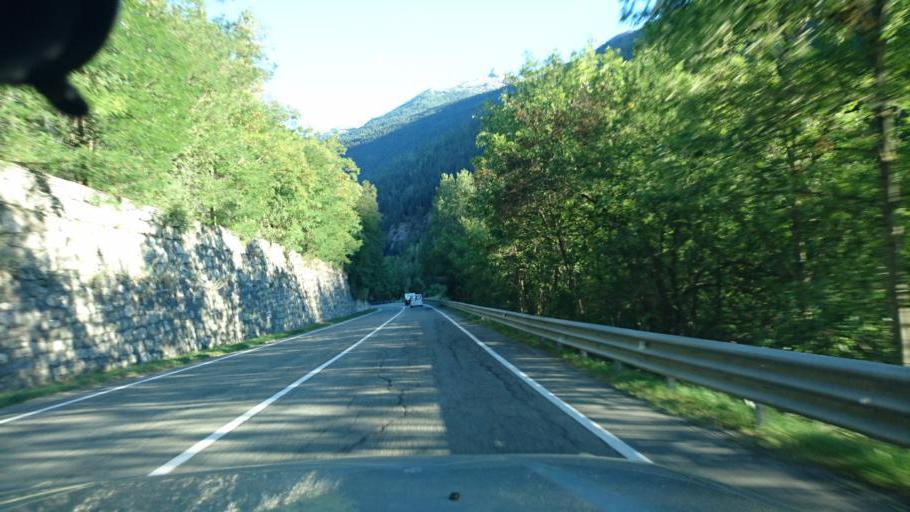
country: IT
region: Aosta Valley
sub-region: Valle d'Aosta
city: La Salle
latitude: 45.7399
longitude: 7.0686
